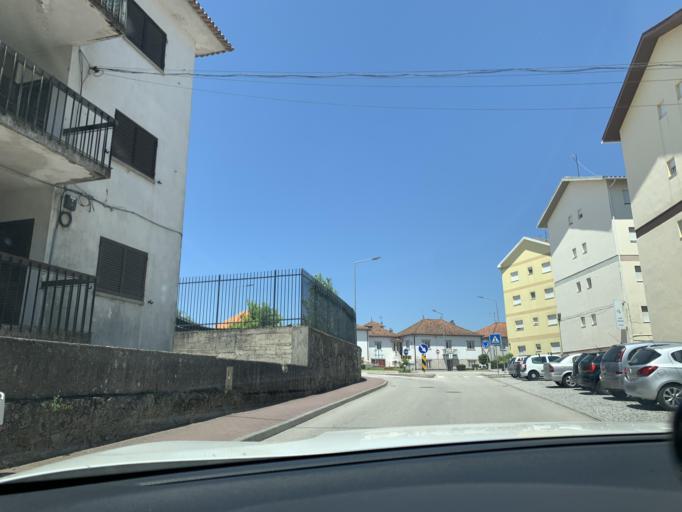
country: PT
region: Viseu
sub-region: Mangualde
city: Mangualde
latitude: 40.6062
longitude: -7.7641
